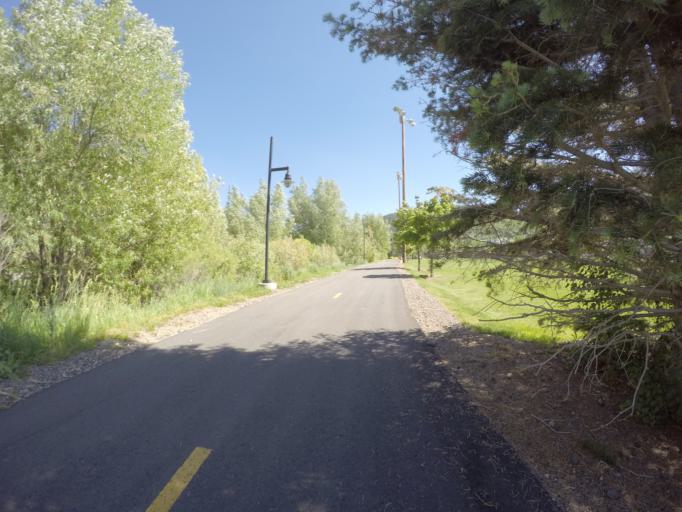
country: US
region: Utah
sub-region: Summit County
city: Park City
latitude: 40.6557
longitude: -111.5031
